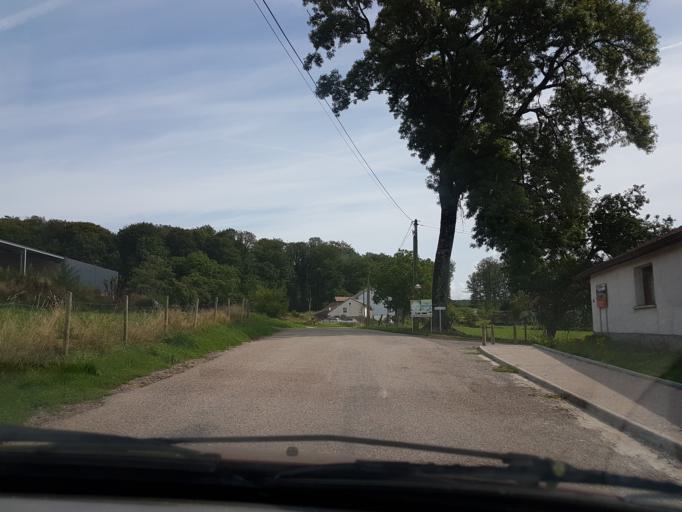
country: FR
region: Franche-Comte
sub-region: Departement de la Haute-Saone
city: Fougerolles
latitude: 47.8726
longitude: 6.4742
